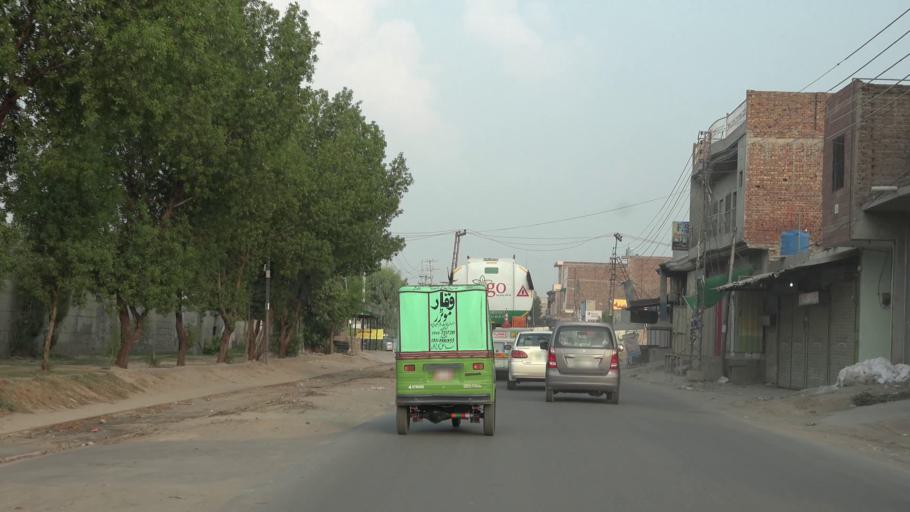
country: PK
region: Punjab
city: Faisalabad
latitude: 31.4494
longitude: 73.1236
